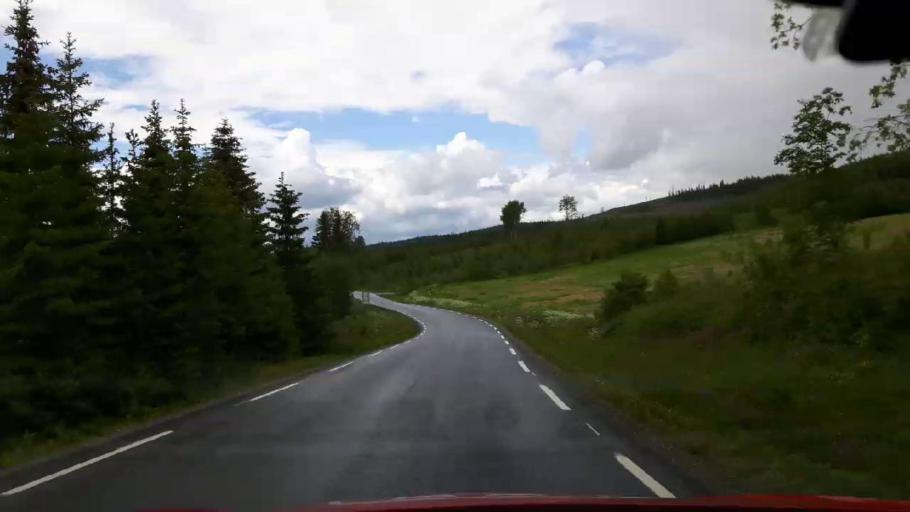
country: NO
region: Nord-Trondelag
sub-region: Lierne
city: Sandvika
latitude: 64.0974
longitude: 14.0345
